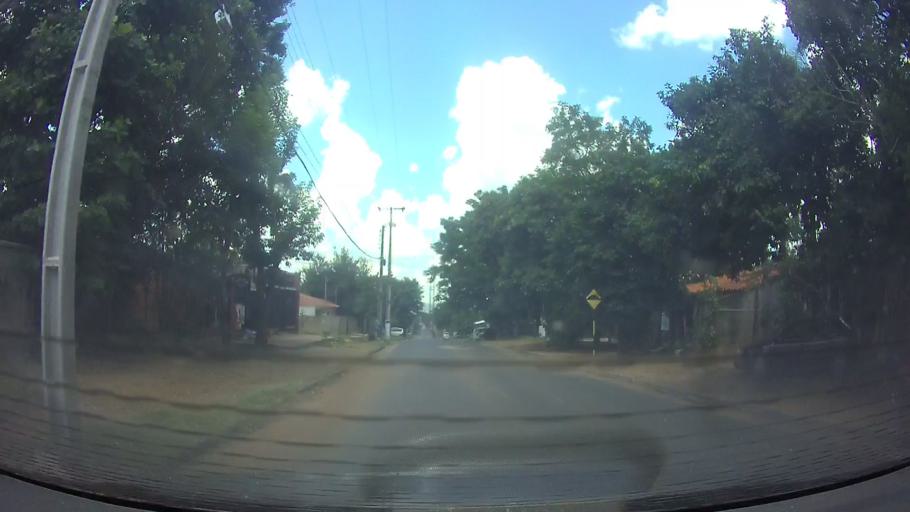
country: PY
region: Central
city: Limpio
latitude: -25.1676
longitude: -57.4382
